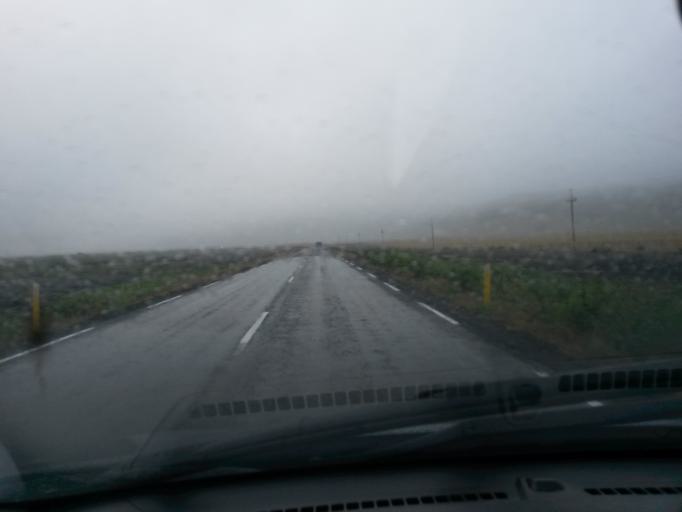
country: IS
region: South
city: Vestmannaeyjar
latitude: 63.5132
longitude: -19.4555
